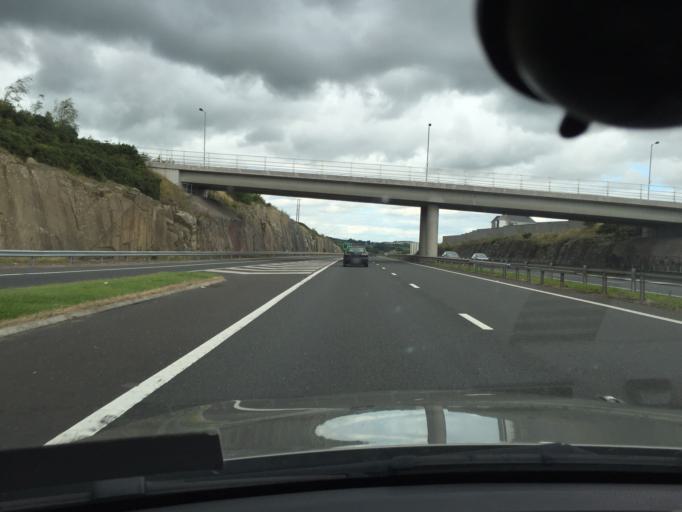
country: GB
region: Northern Ireland
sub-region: Newry and Mourne District
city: Newry
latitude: 54.1879
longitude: -6.3612
